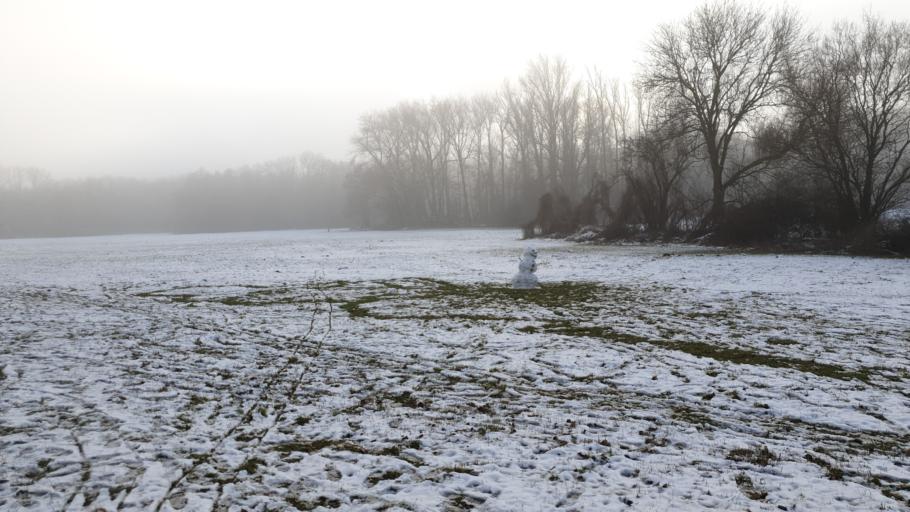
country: DE
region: Saxony
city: Taucha
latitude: 51.3956
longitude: 12.4737
